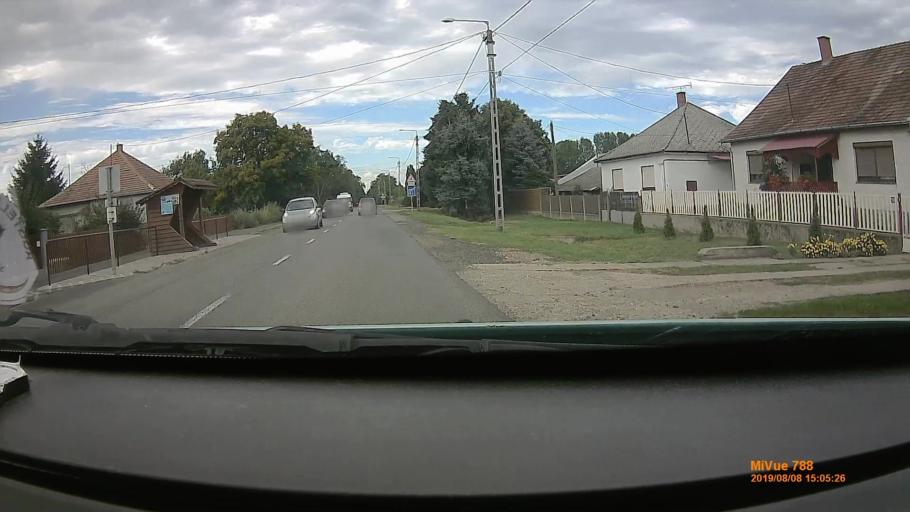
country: HU
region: Szabolcs-Szatmar-Bereg
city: Kocsord
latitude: 47.9415
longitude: 22.4280
